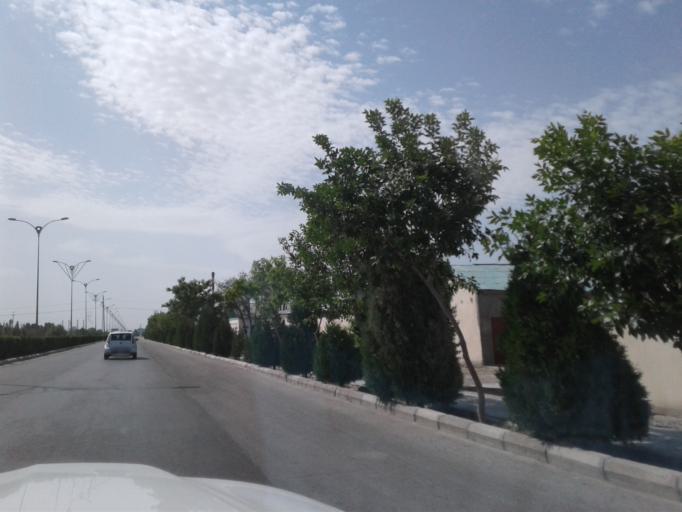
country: TM
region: Dasoguz
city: Dasoguz
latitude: 41.8316
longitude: 59.9406
